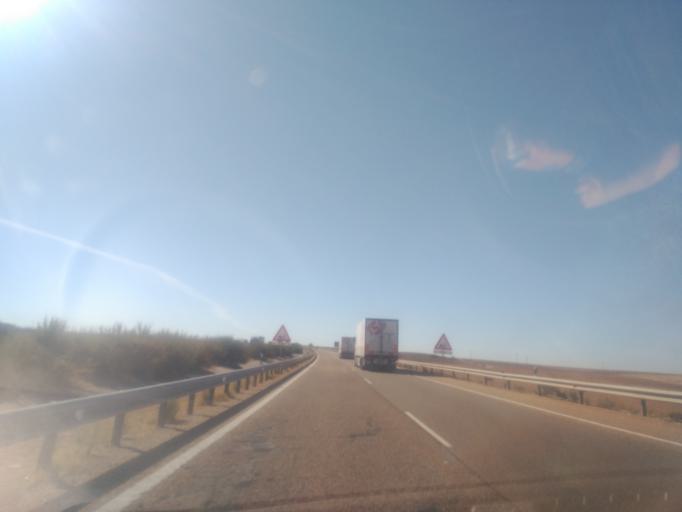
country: ES
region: Castille and Leon
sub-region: Provincia de Valladolid
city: Pollos
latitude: 41.4061
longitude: -5.1363
